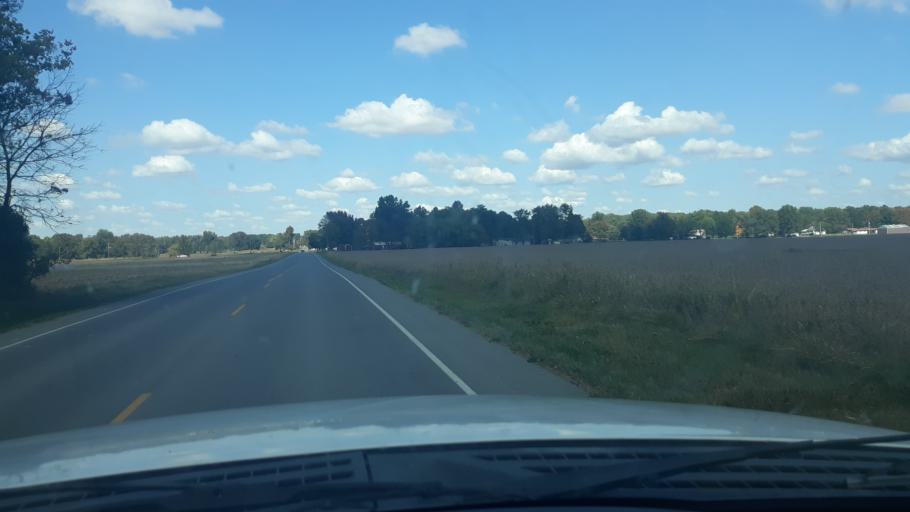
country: US
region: Illinois
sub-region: Saline County
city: Eldorado
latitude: 37.8161
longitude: -88.4848
